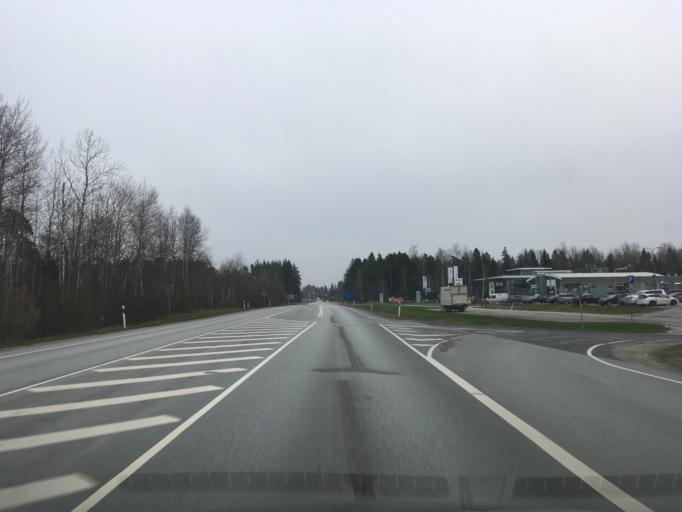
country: EE
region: Ida-Virumaa
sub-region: Johvi vald
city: Johvi
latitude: 59.3641
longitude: 27.4506
